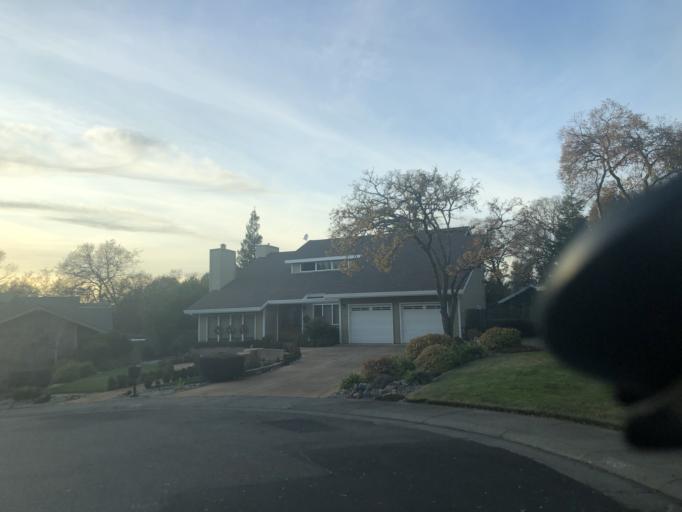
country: US
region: California
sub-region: Sacramento County
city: Gold River
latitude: 38.6431
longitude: -121.2321
